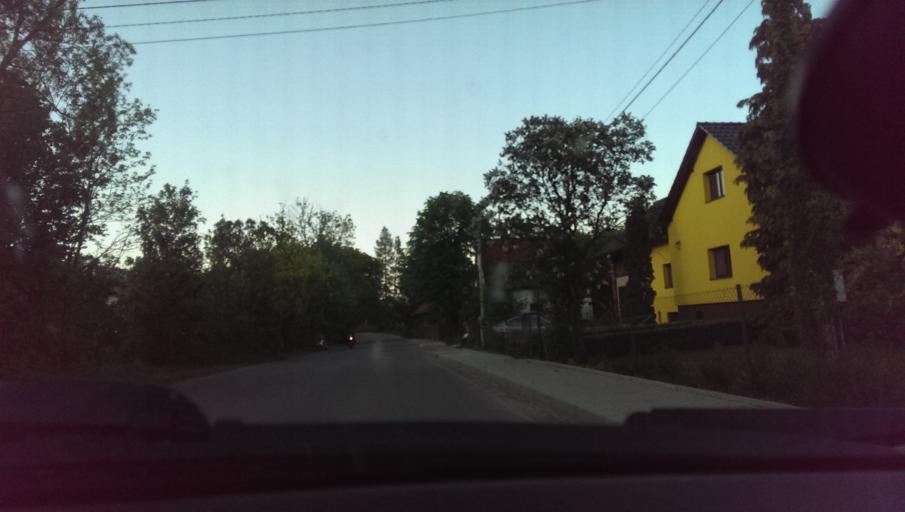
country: CZ
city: Lichnov (o. Novy Jicin)
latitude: 49.5718
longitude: 18.1802
